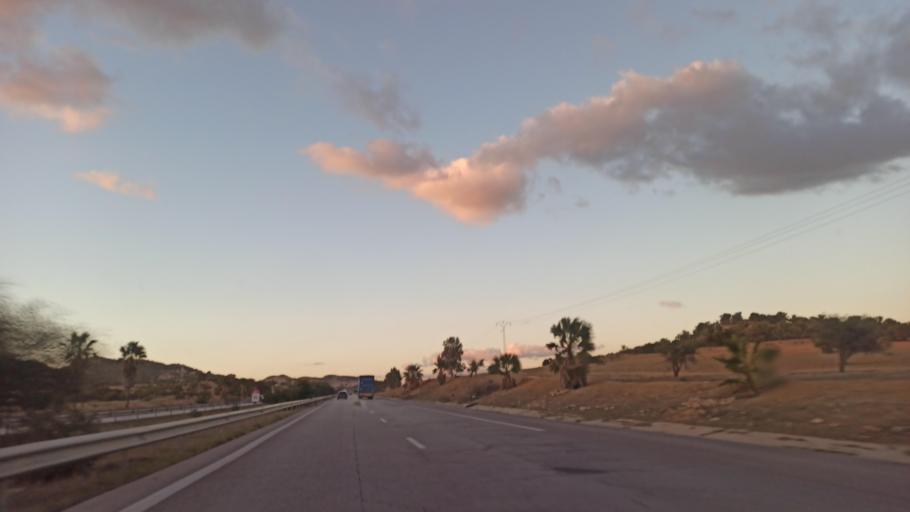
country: TN
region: Susah
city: Harqalah
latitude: 36.2197
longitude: 10.4183
